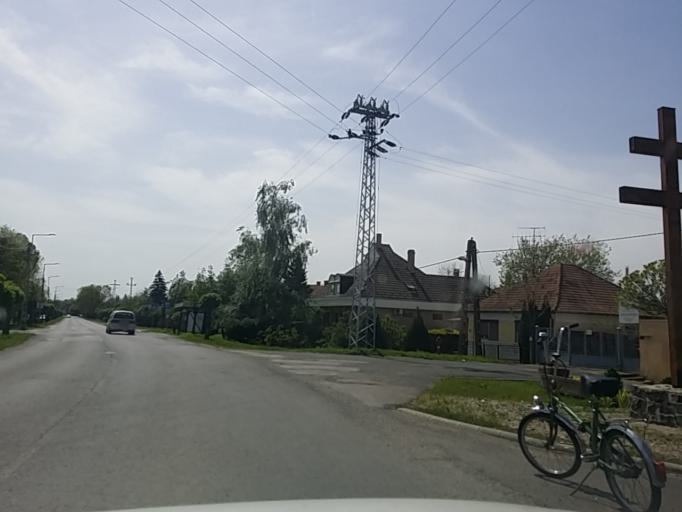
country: HU
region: Bekes
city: Gyula
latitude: 46.6540
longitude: 21.2835
